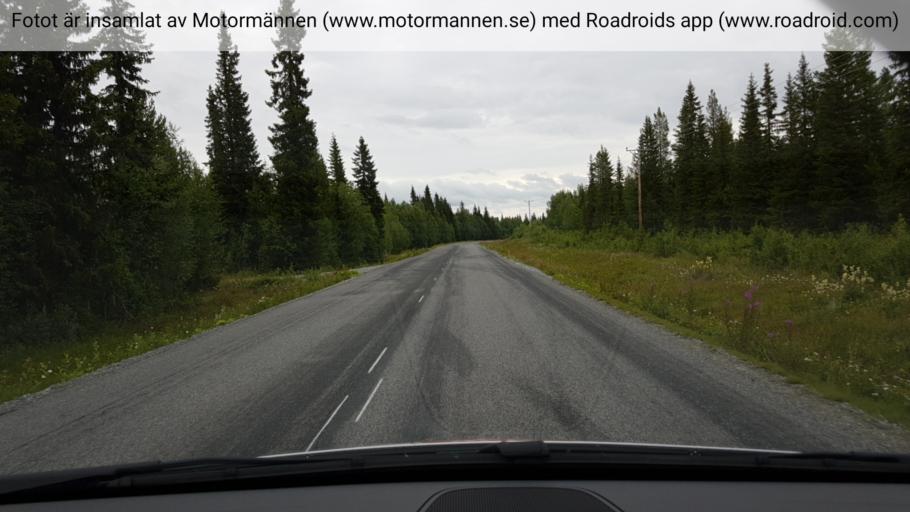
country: SE
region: Jaemtland
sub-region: Krokoms Kommun
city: Krokom
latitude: 63.6614
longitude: 14.4900
